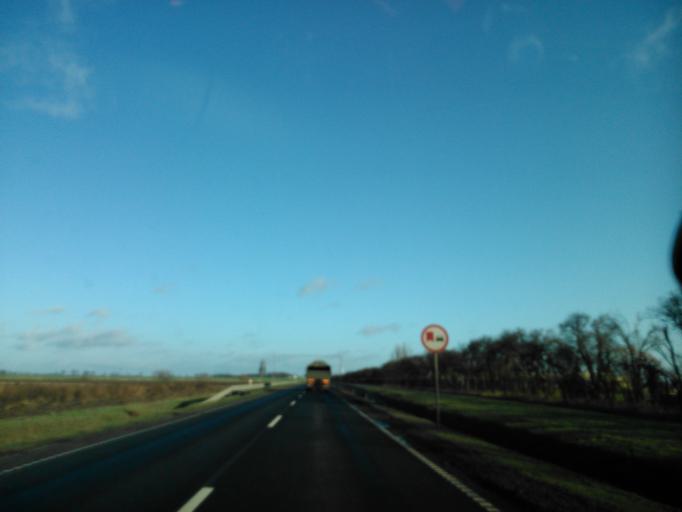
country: PL
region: Kujawsko-Pomorskie
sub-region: Powiat inowroclawski
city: Inowroclaw
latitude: 52.8301
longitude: 18.3113
